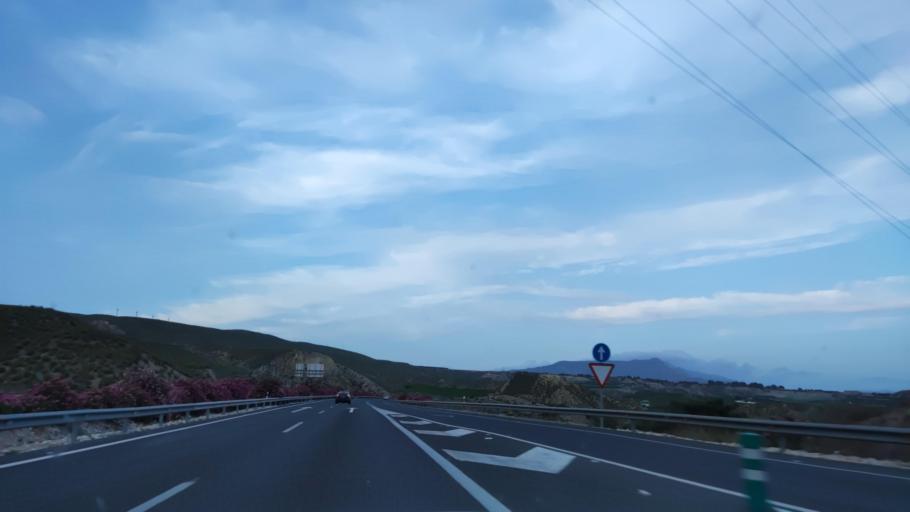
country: ES
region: Murcia
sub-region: Murcia
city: Cieza
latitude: 38.2489
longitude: -1.4092
